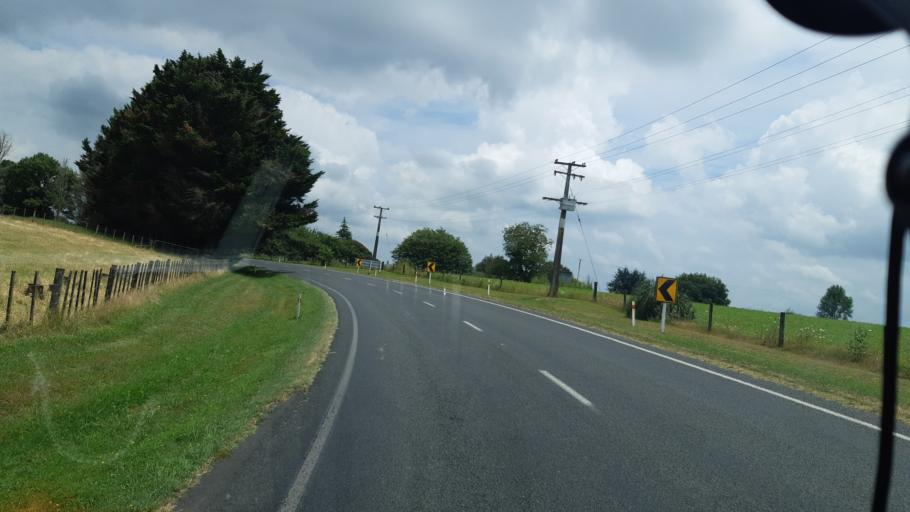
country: NZ
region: Waikato
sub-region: Waipa District
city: Cambridge
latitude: -38.0483
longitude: 175.3927
